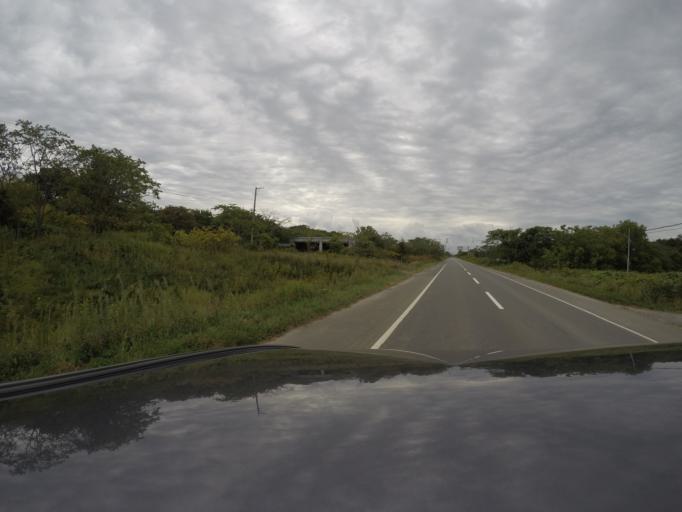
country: JP
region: Hokkaido
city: Makubetsu
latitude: 45.1958
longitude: 141.7394
